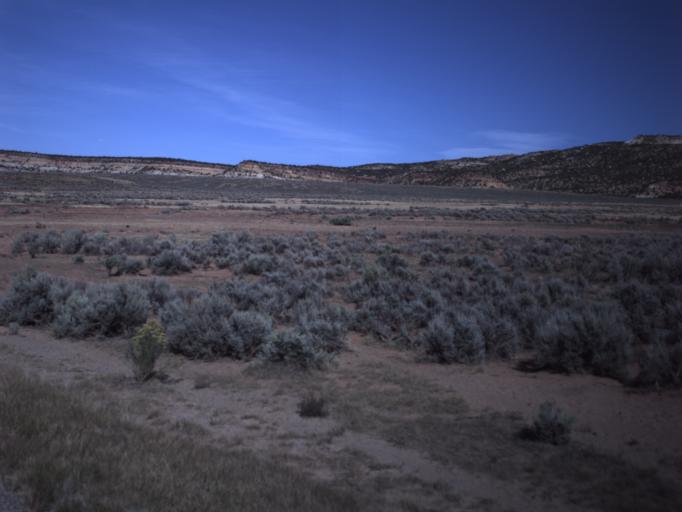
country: US
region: Utah
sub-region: San Juan County
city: Monticello
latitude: 38.0164
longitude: -109.4310
